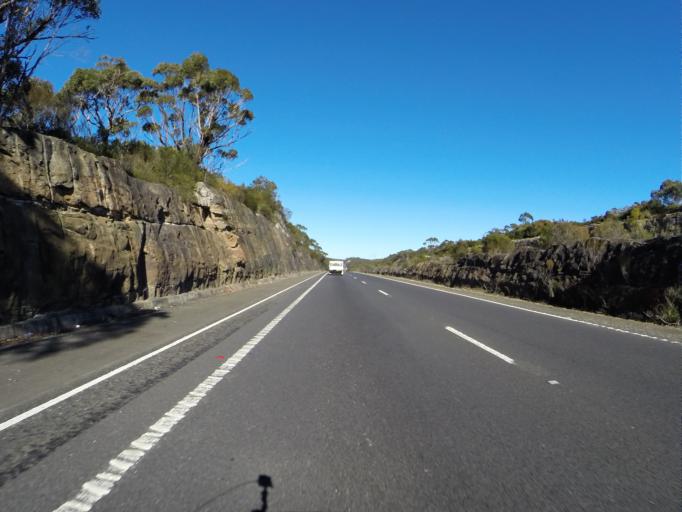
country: AU
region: New South Wales
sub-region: Wollongong
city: Helensburgh
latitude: -34.2106
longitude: 150.9610
